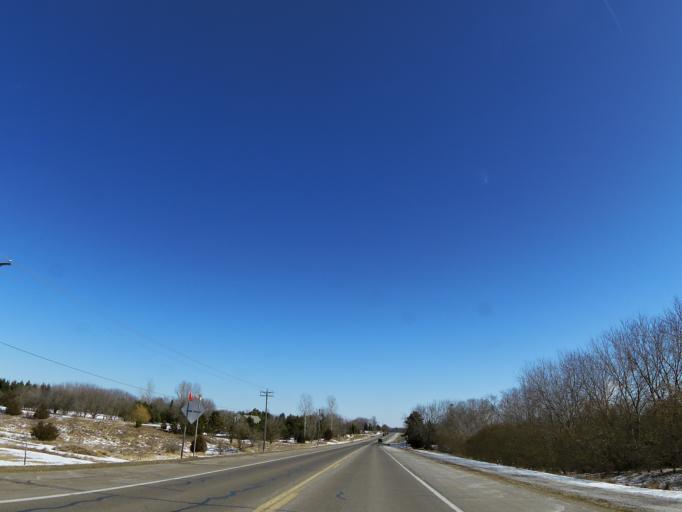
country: US
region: Minnesota
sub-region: Washington County
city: Grant
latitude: 45.0577
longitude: -92.8809
